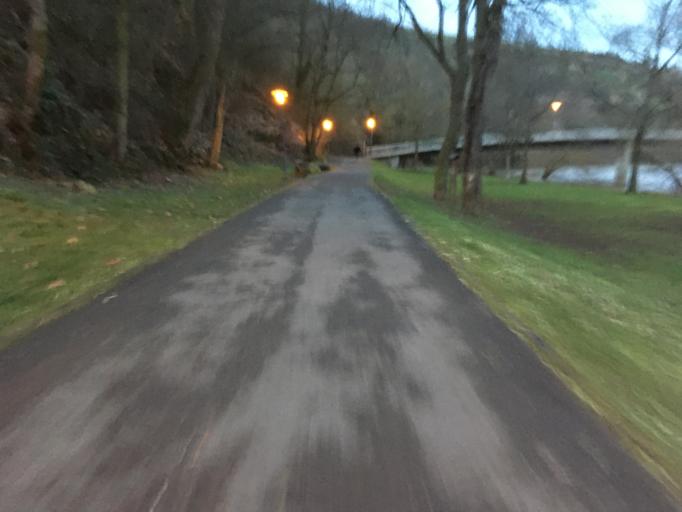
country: DE
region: Rheinland-Pfalz
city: Bad Kreuznach
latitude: 49.8410
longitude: 7.8515
